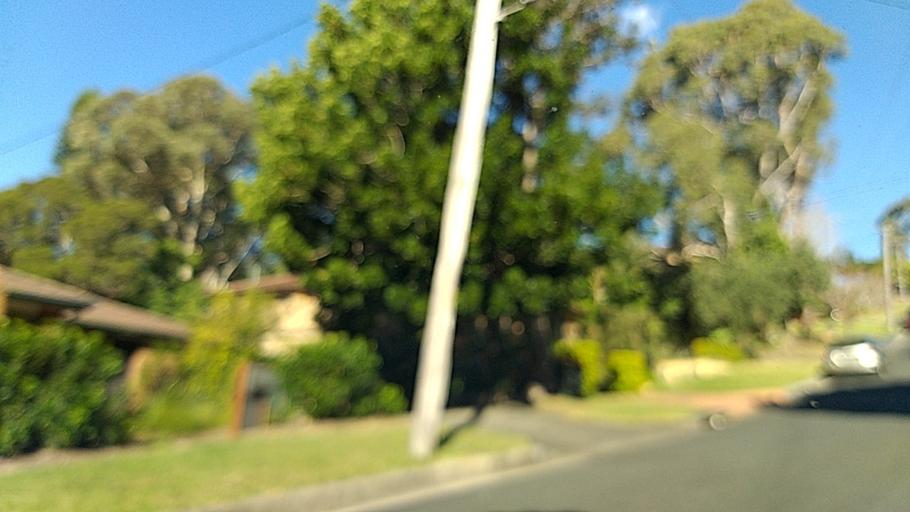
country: AU
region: New South Wales
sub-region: Wollongong
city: Mount Keira
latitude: -34.4180
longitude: 150.8524
